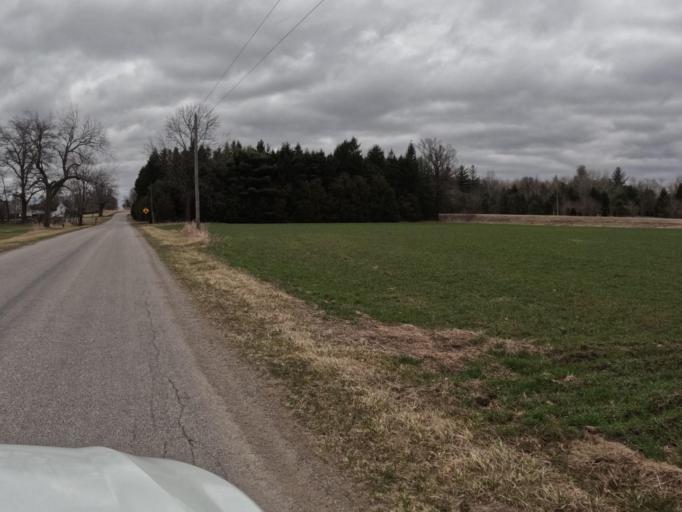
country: CA
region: Ontario
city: Norfolk County
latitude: 42.9393
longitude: -80.4280
